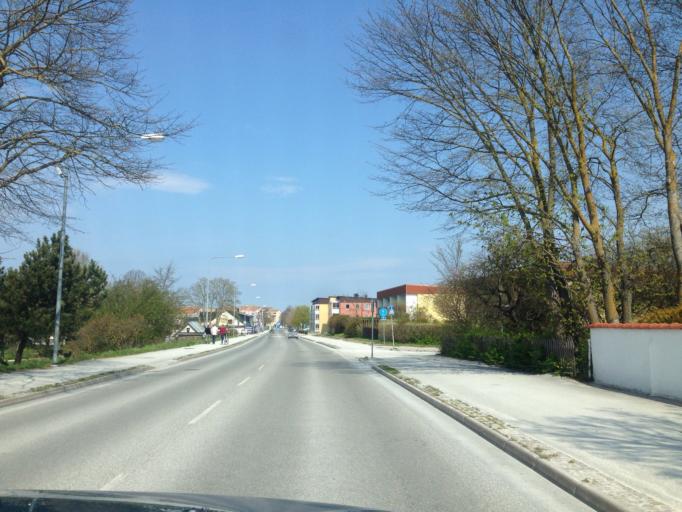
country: SE
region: Gotland
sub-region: Gotland
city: Visby
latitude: 57.6267
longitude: 18.2870
